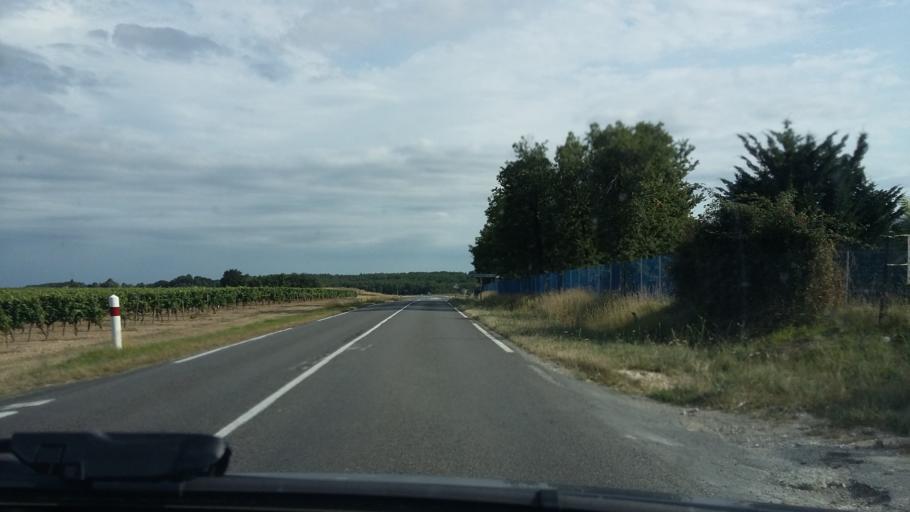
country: FR
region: Poitou-Charentes
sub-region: Departement de la Charente
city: Asnieres-sur-Nouere
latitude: 45.7271
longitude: 0.0642
